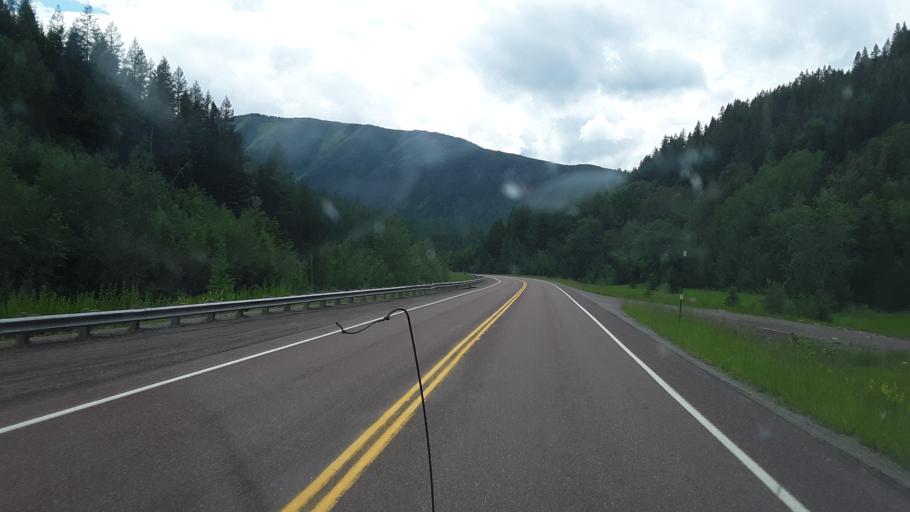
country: US
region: Montana
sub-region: Flathead County
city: Bigfork
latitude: 48.2356
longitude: -113.5348
